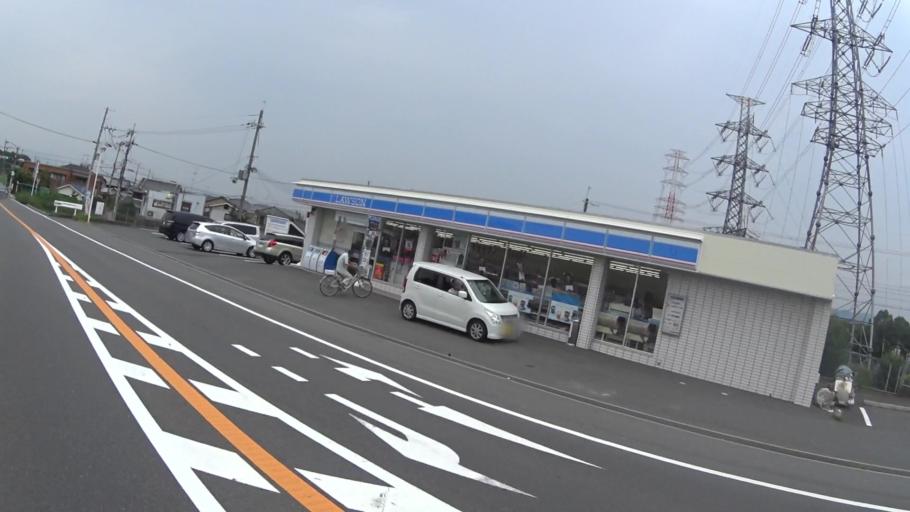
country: JP
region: Kyoto
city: Tanabe
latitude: 34.8323
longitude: 135.7553
